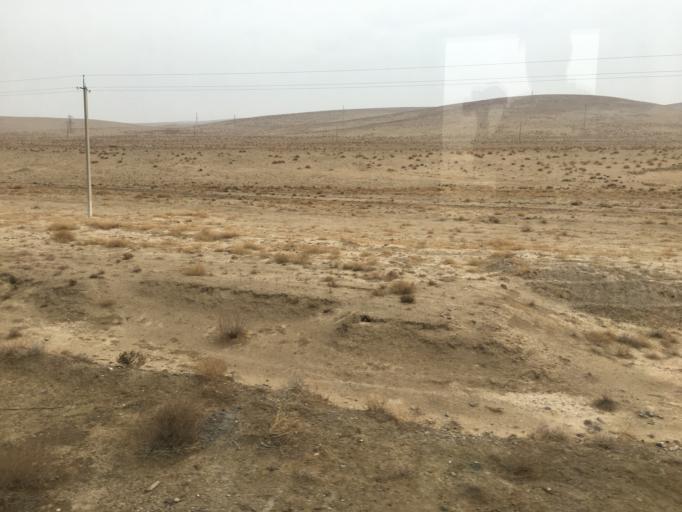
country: TM
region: Mary
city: Serhetabat
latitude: 35.4890
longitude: 62.4462
